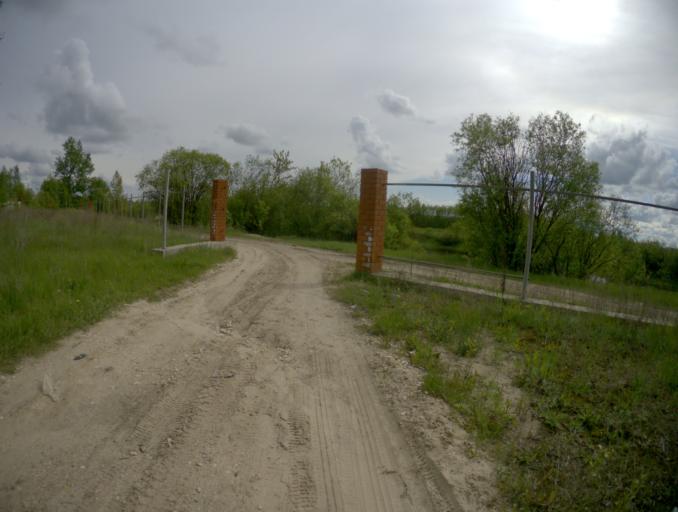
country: RU
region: Rjazan
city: Gus'-Zheleznyy
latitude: 55.0007
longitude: 41.1908
